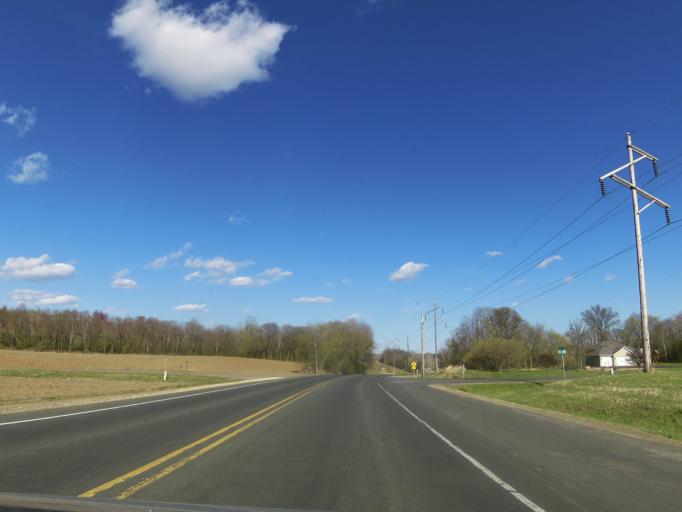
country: US
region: Wisconsin
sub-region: Saint Croix County
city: Somerset
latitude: 45.0355
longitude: -92.6732
